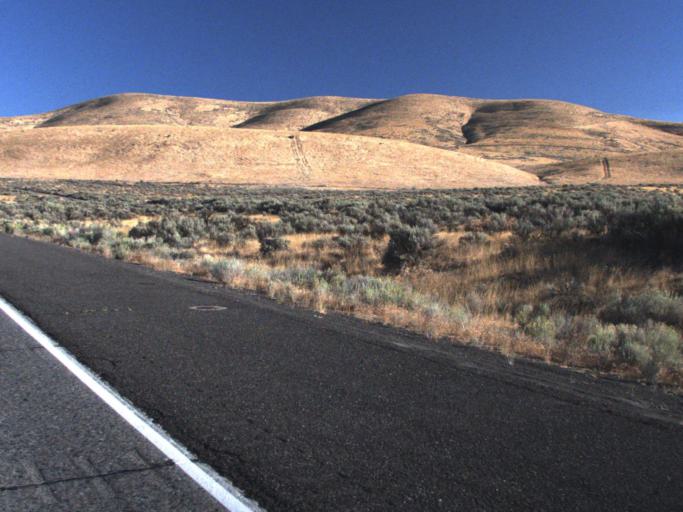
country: US
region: Washington
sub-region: Kittitas County
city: Kittitas
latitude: 46.8396
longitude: -120.3714
